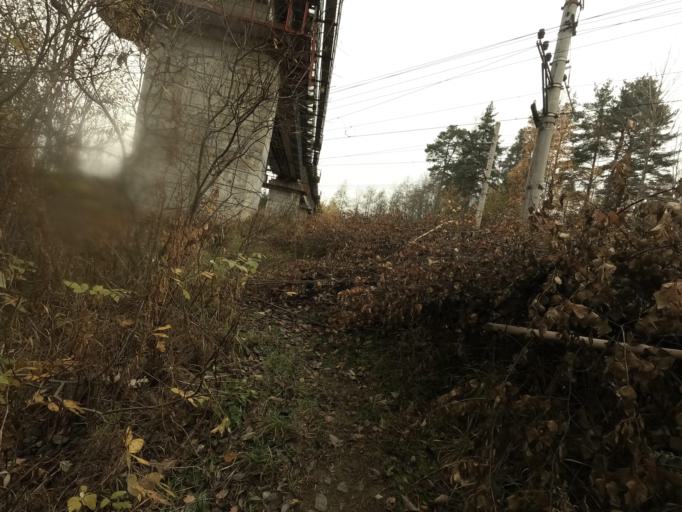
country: RU
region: Leningrad
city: Pavlovo
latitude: 59.7714
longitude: 30.9064
